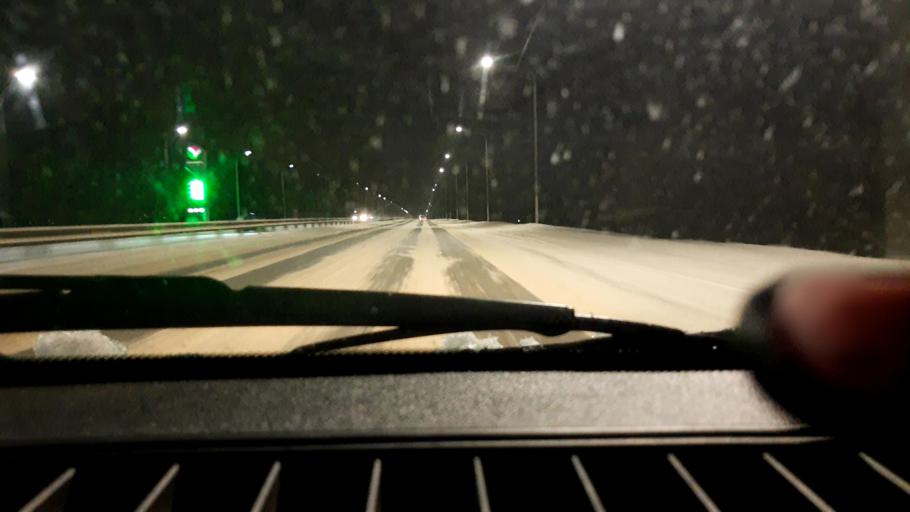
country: RU
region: Bashkortostan
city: Ufa
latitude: 54.5256
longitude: 55.8998
